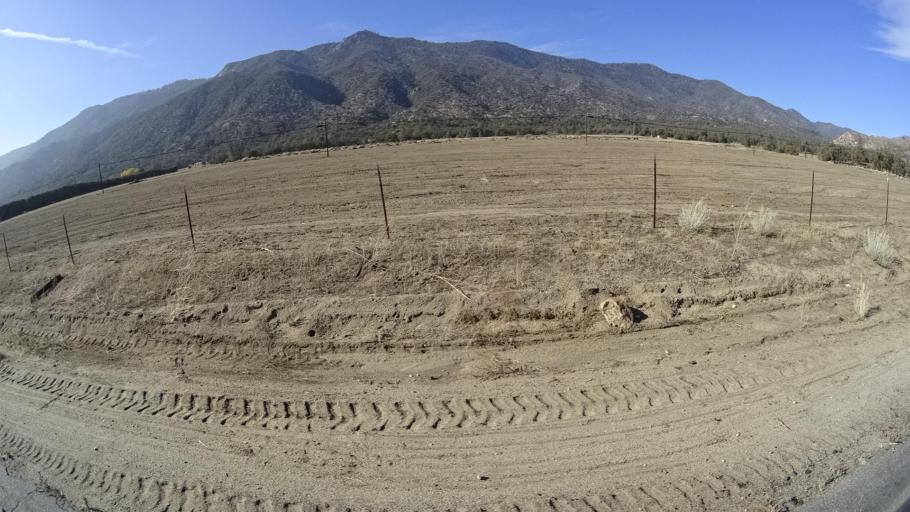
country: US
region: California
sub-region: Kern County
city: Bodfish
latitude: 35.4294
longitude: -118.5339
